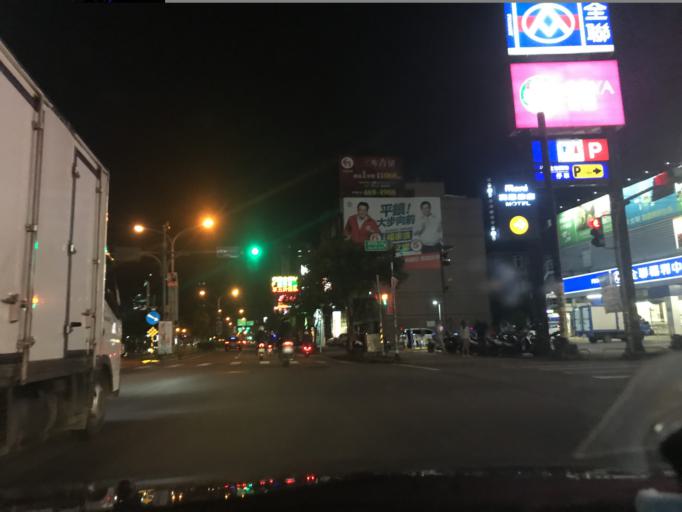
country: TW
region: Taiwan
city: Daxi
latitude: 24.9402
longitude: 121.2190
